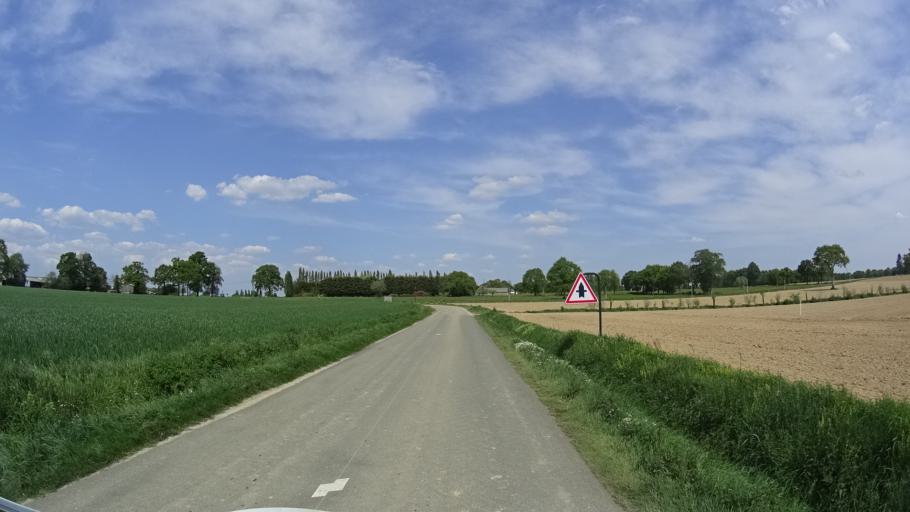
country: FR
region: Brittany
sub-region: Departement d'Ille-et-Vilaine
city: Torce
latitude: 48.0435
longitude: -1.2643
